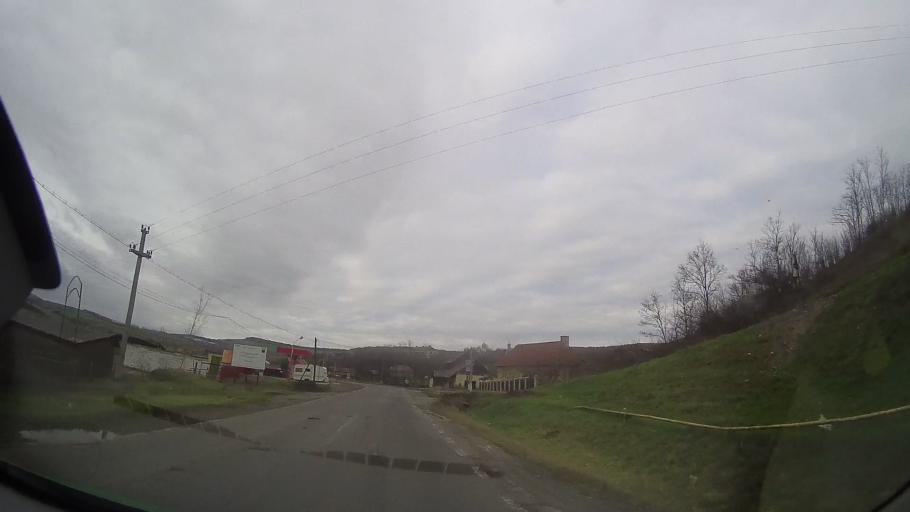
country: RO
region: Bistrita-Nasaud
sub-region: Comuna Urmenis
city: Urmenis
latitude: 46.7666
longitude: 24.3699
